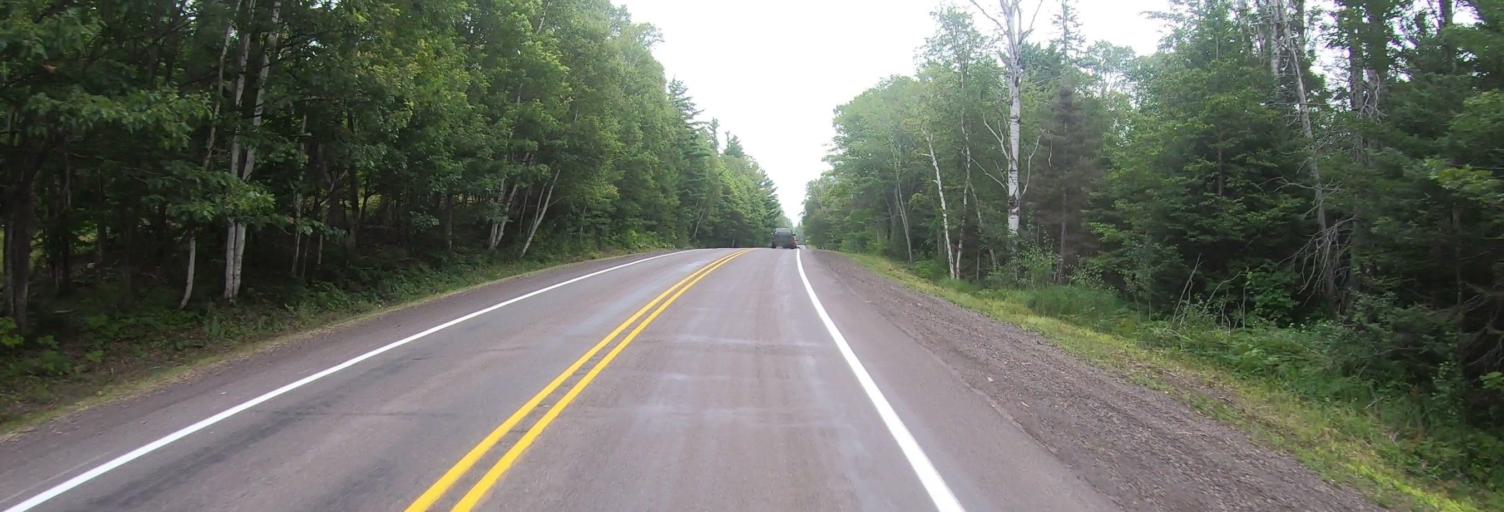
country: US
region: Michigan
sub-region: Keweenaw County
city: Eagle River
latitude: 47.4016
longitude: -88.2389
